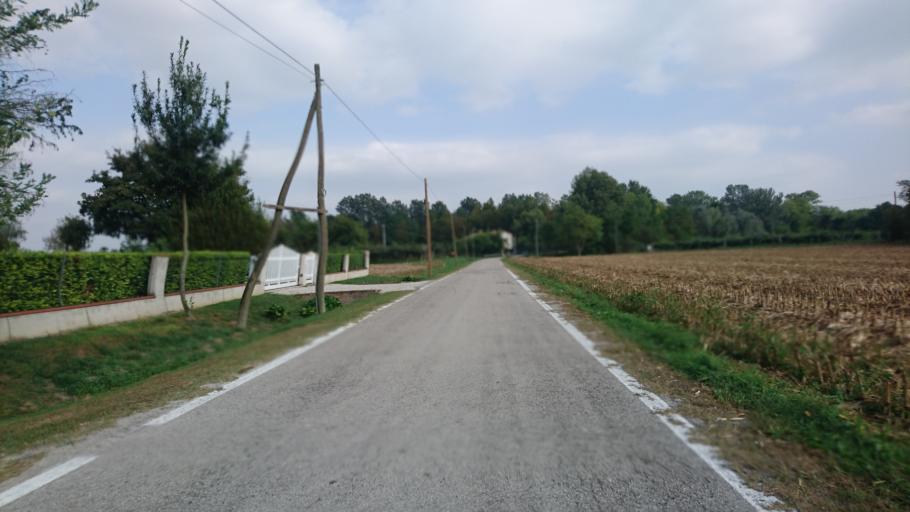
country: IT
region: Veneto
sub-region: Provincia di Padova
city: Piazzola sul Brenta
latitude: 45.5700
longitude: 11.7771
